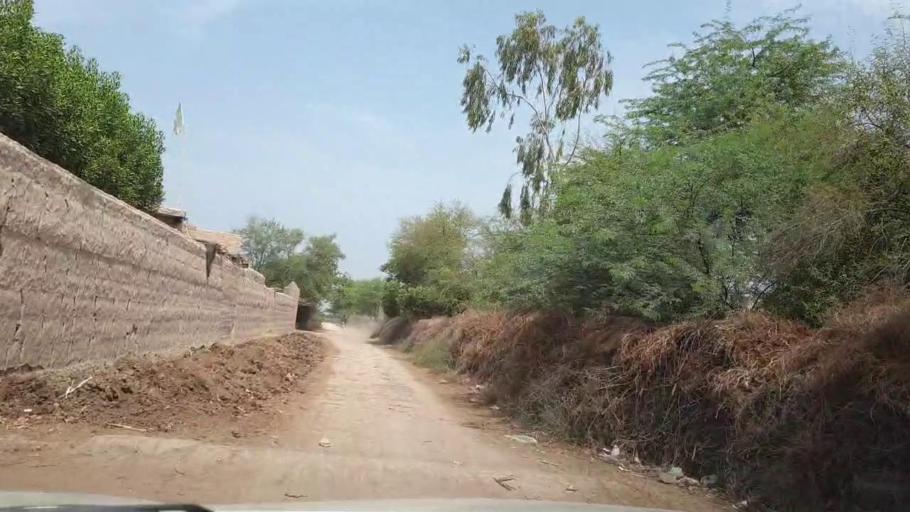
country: PK
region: Sindh
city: Sobhadero
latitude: 27.3870
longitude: 68.2751
